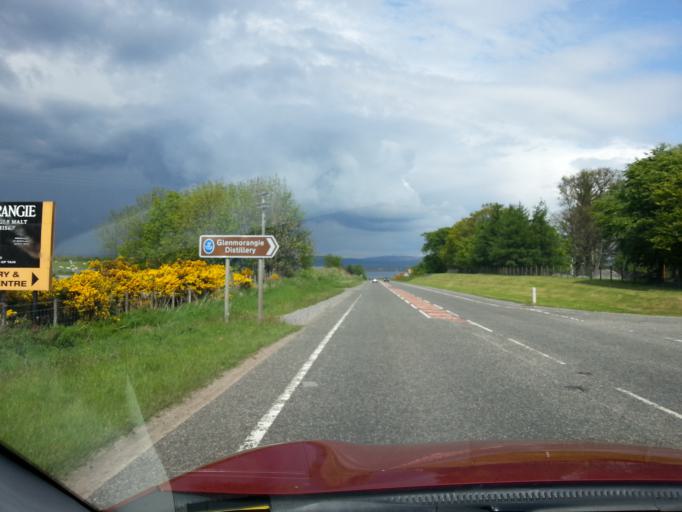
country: GB
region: Scotland
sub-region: Highland
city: Tain
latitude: 57.8234
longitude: -4.0777
